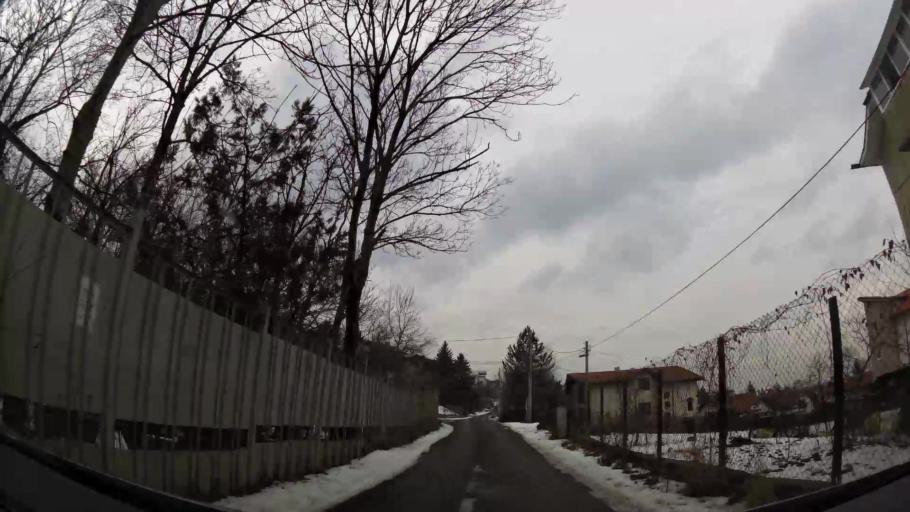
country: BG
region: Sofiya
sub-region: Obshtina Bozhurishte
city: Bozhurishte
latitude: 42.6784
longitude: 23.2327
